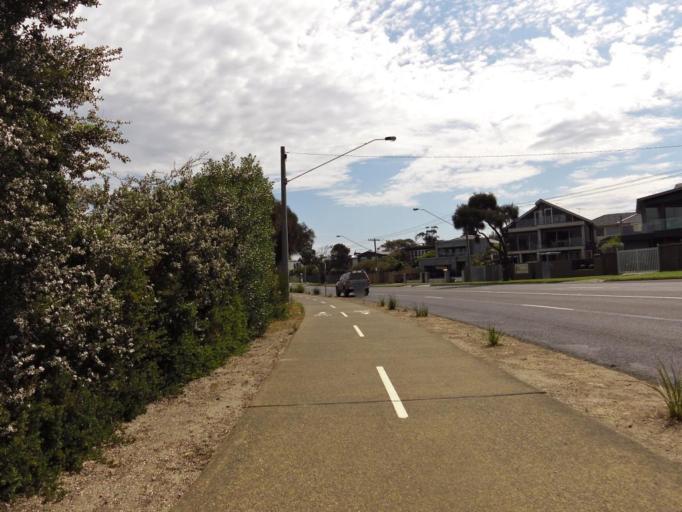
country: AU
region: Victoria
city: Beaumaris
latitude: -37.9881
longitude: 145.0276
